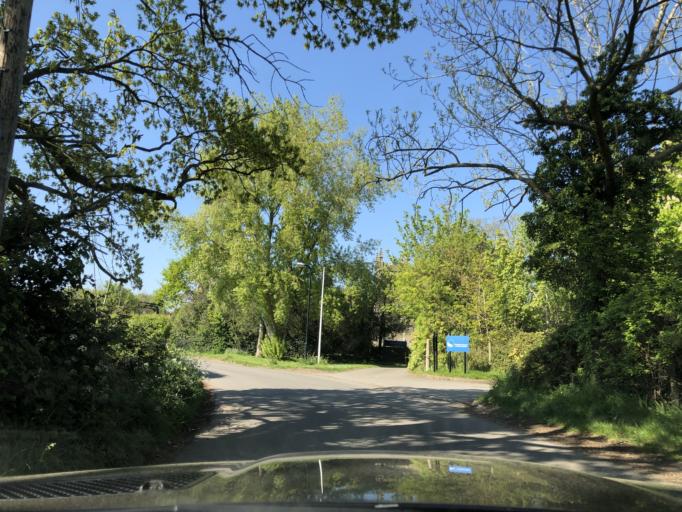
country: GB
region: England
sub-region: Warwickshire
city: Warwick
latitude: 52.2868
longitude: -1.6227
